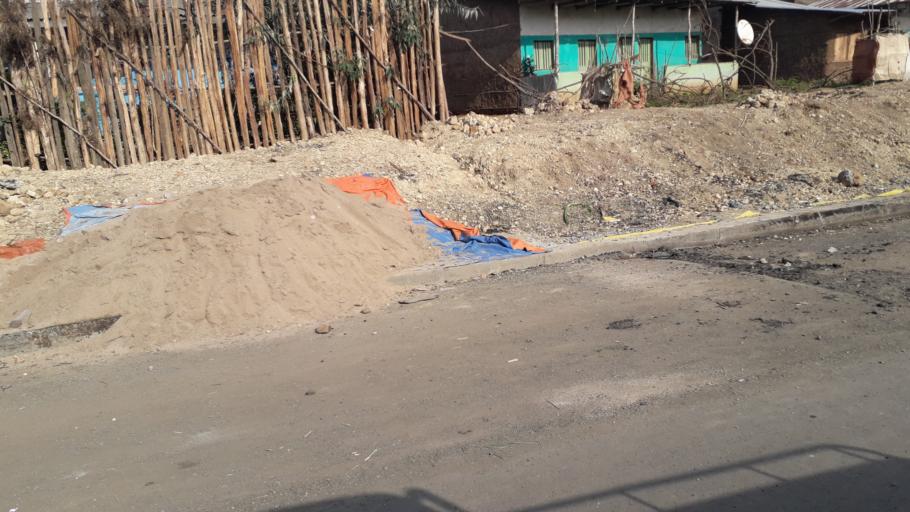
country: ET
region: Southern Nations, Nationalities, and People's Region
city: Mizan Teferi
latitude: 6.9363
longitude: 35.4995
